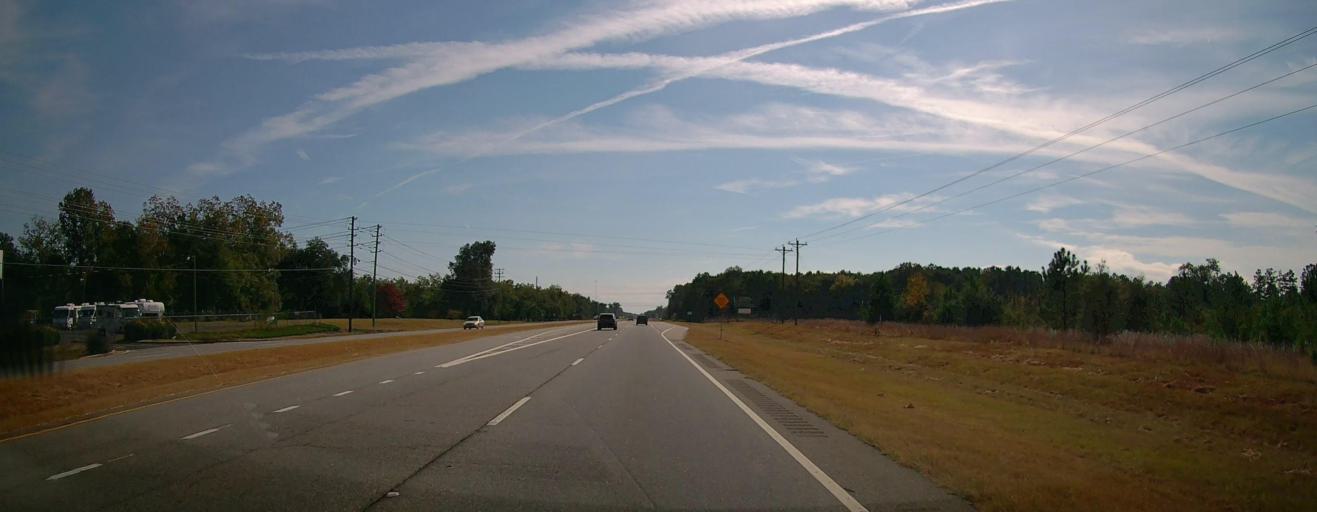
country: US
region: Georgia
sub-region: Dougherty County
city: Putney
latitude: 31.5193
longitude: -84.1157
